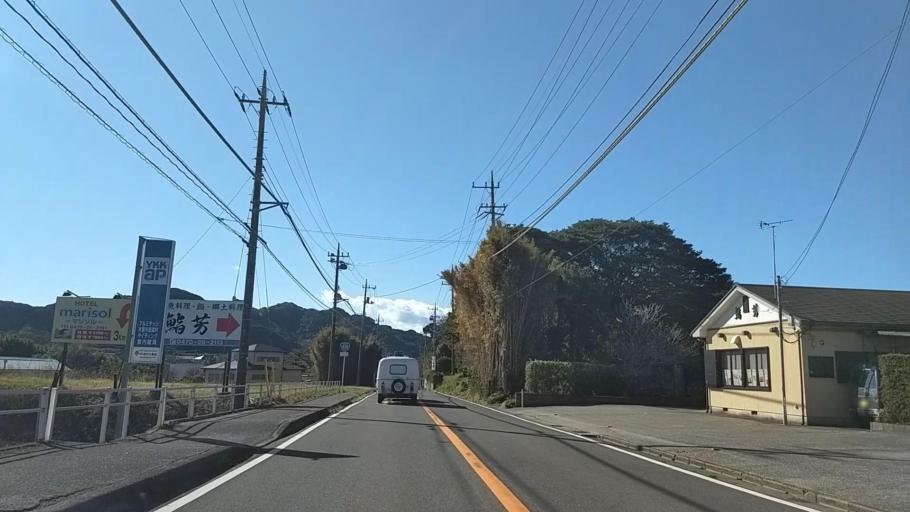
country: JP
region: Chiba
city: Tateyama
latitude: 34.9306
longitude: 139.8378
